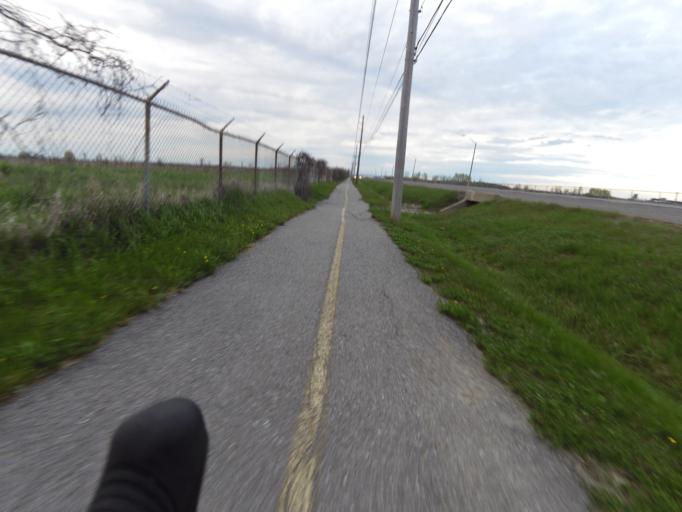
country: CA
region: Ontario
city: Bells Corners
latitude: 45.2969
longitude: -75.7624
